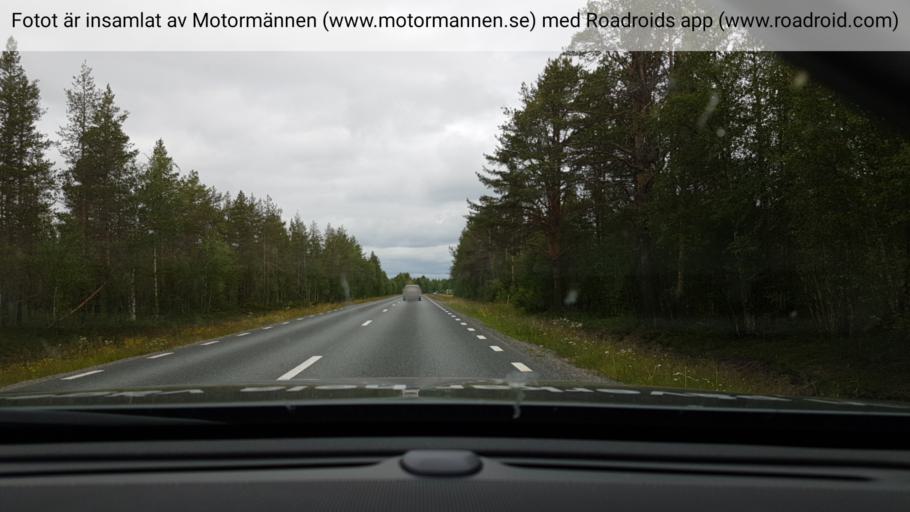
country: SE
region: Vaesterbotten
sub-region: Sorsele Kommun
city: Sorsele
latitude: 65.5070
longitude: 17.5433
